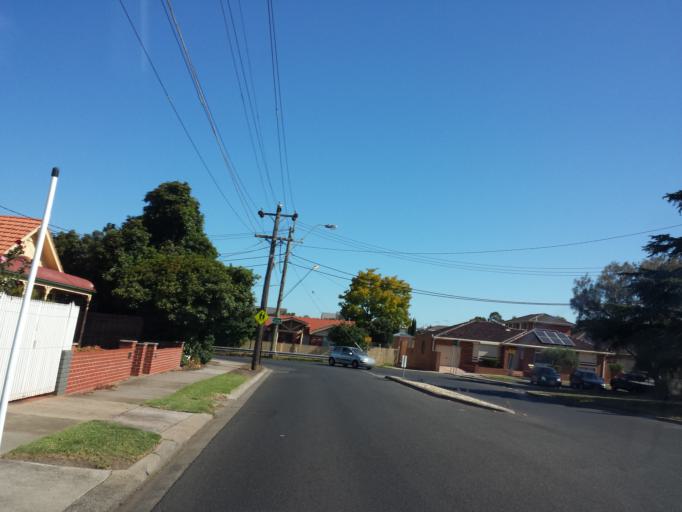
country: AU
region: Victoria
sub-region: Moonee Valley
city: Moonee Ponds
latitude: -37.7665
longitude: 144.9055
